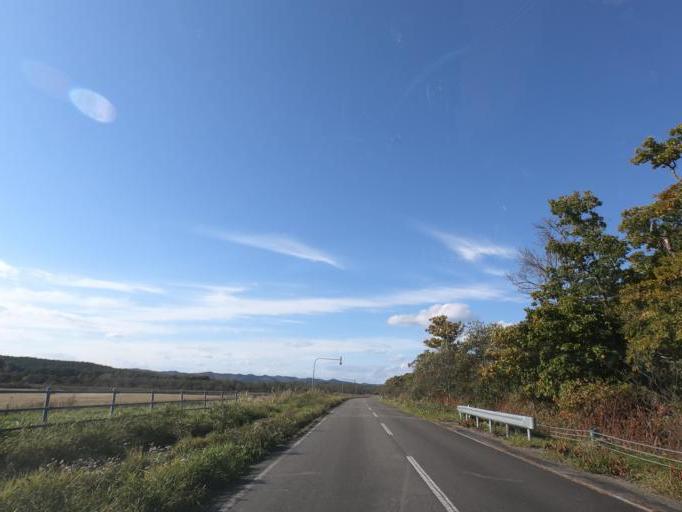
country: JP
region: Hokkaido
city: Obihiro
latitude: 42.6337
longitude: 143.5196
